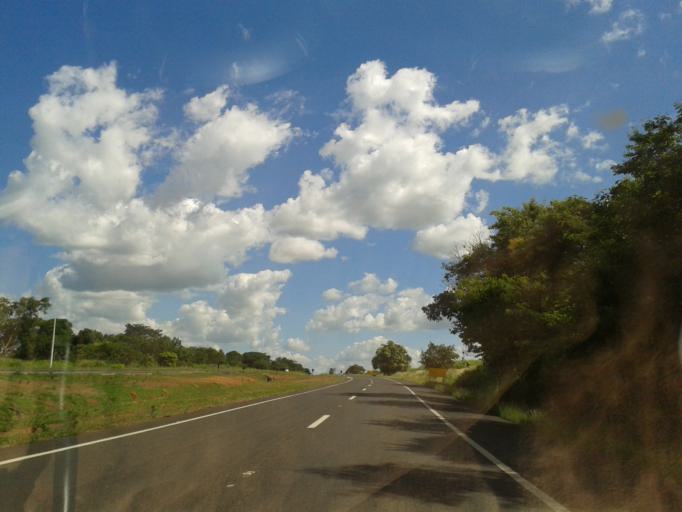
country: BR
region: Goias
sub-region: Morrinhos
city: Morrinhos
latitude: -17.6565
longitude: -49.1698
